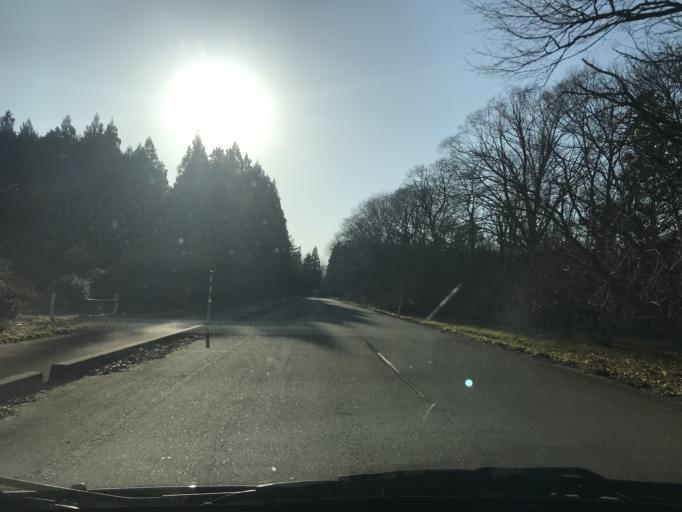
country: JP
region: Iwate
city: Kitakami
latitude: 39.2377
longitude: 141.0493
